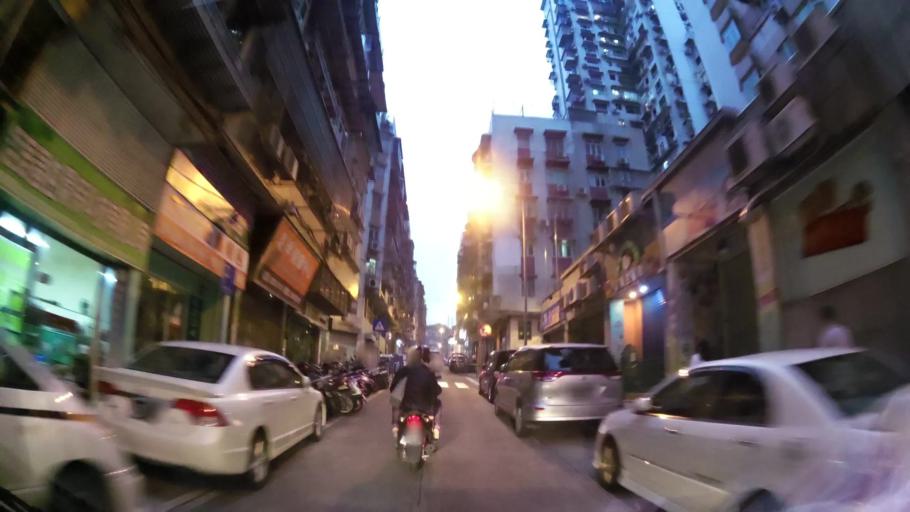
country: MO
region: Macau
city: Macau
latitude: 22.1994
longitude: 113.5450
